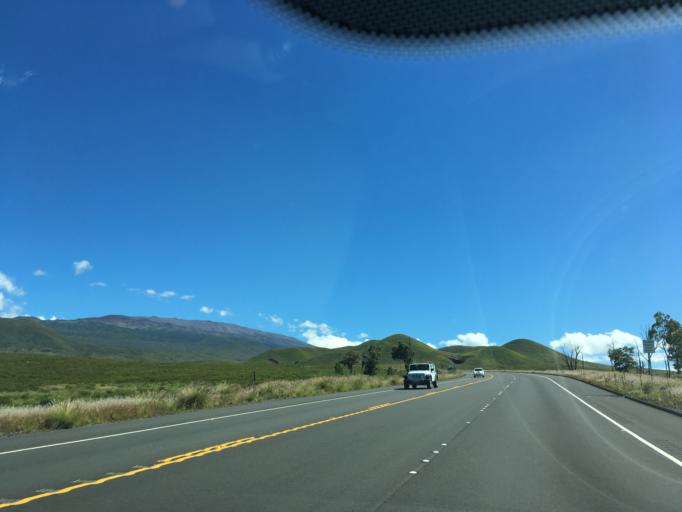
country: US
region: Hawaii
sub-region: Hawaii County
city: Waikoloa
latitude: 19.7902
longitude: -155.6566
